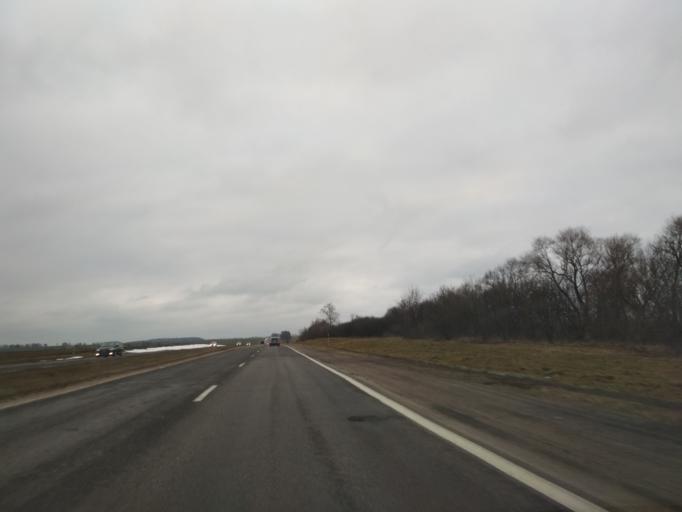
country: BY
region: Minsk
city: Blon'
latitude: 53.5634
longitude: 28.1446
